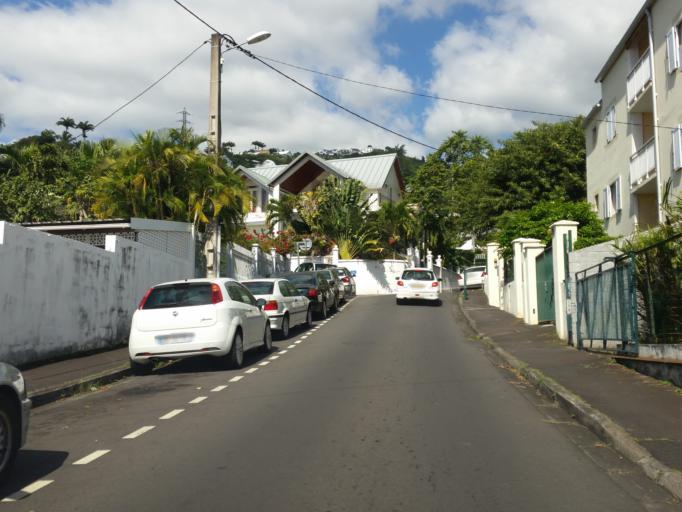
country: RE
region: Reunion
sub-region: Reunion
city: Saint-Denis
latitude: -20.8982
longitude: 55.4561
